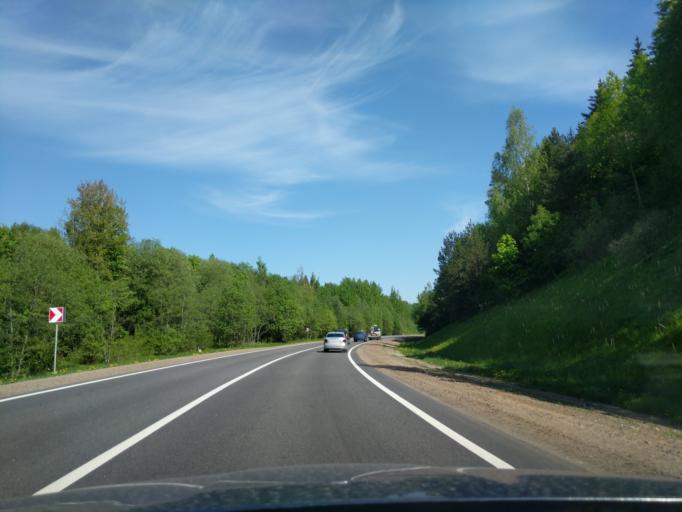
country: BY
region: Minsk
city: Bal'shavik
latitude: 54.1056
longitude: 27.5295
